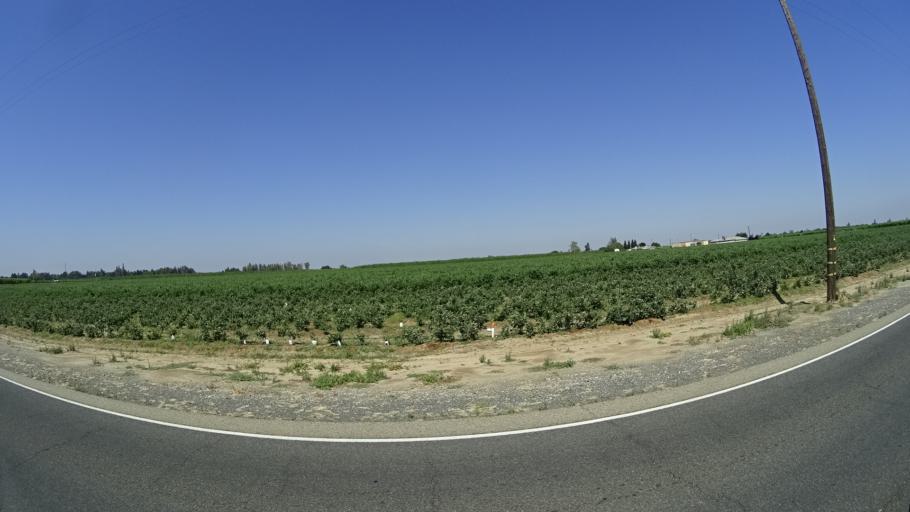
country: US
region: California
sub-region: Fresno County
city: Kingsburg
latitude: 36.4577
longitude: -119.5646
